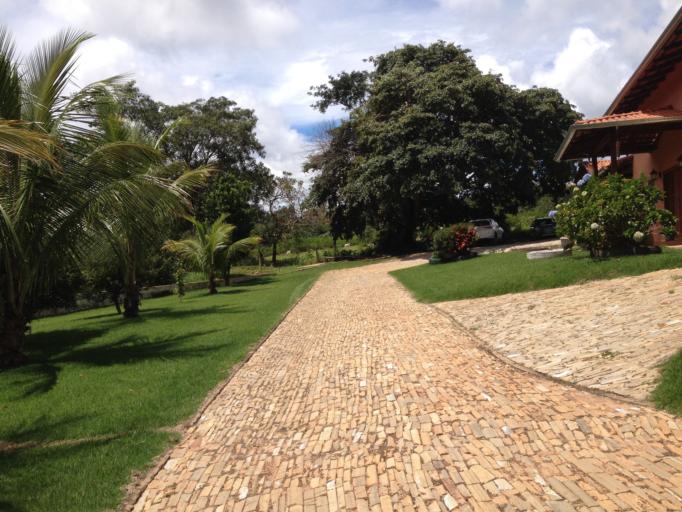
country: BR
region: Goias
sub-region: Pirenopolis
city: Pirenopolis
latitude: -15.9025
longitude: -49.0282
